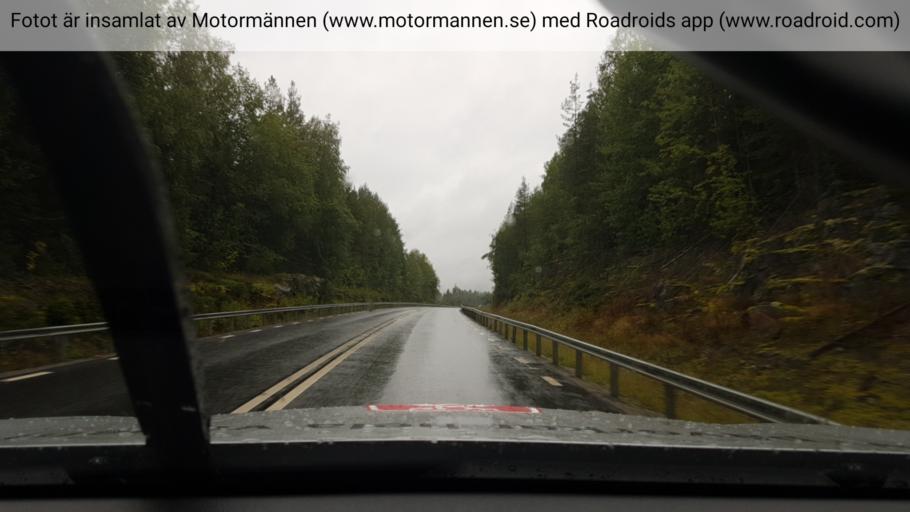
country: SE
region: Vaesterbotten
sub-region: Bjurholms Kommun
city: Bjurholm
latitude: 63.9189
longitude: 19.1815
